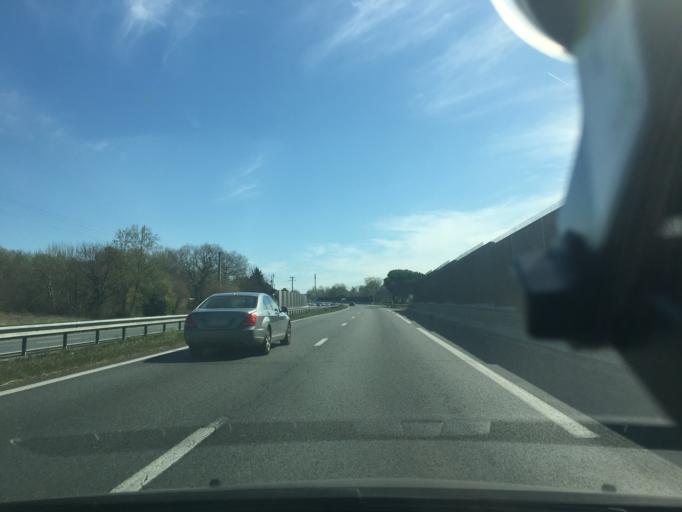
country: FR
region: Aquitaine
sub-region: Departement de la Gironde
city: Lormont
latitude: 44.8668
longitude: -0.4886
